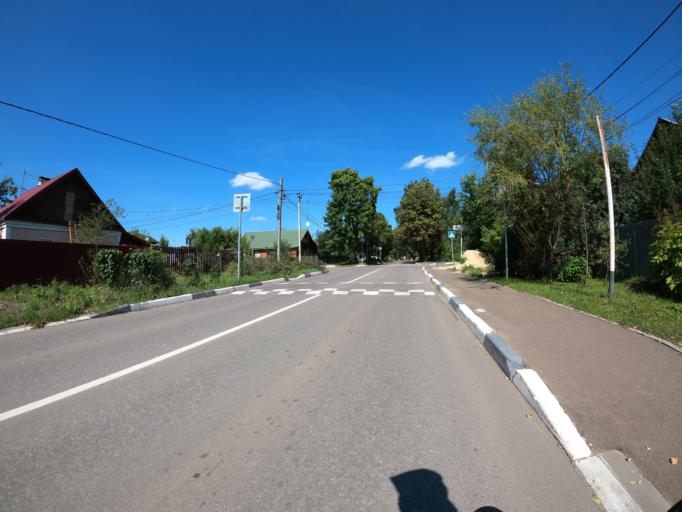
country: RU
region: Moskovskaya
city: Stupino
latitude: 54.8934
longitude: 38.0885
